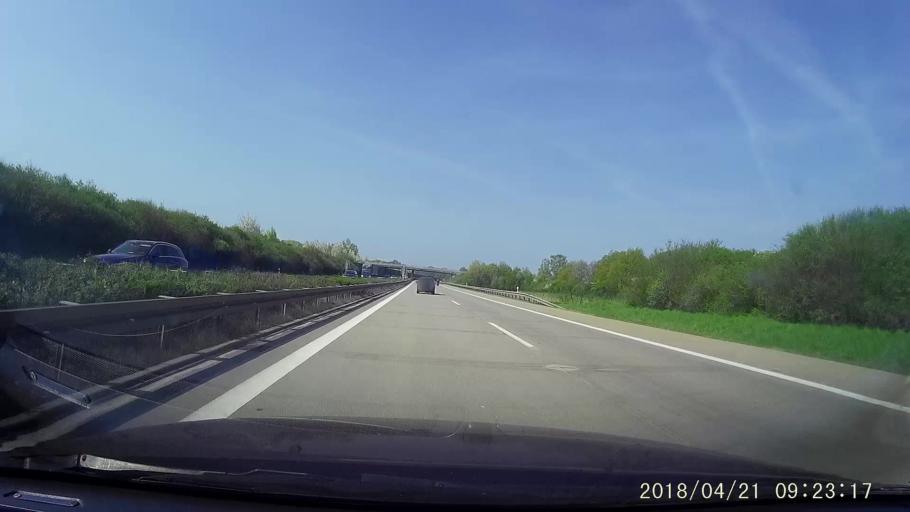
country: DE
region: Saxony
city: Malschwitz
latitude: 51.2080
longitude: 14.5350
